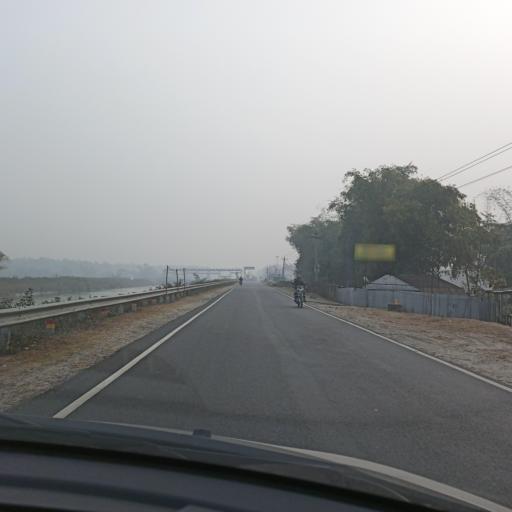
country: IN
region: West Bengal
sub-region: Darjiling
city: Shiliguri
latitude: 26.6811
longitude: 88.5590
